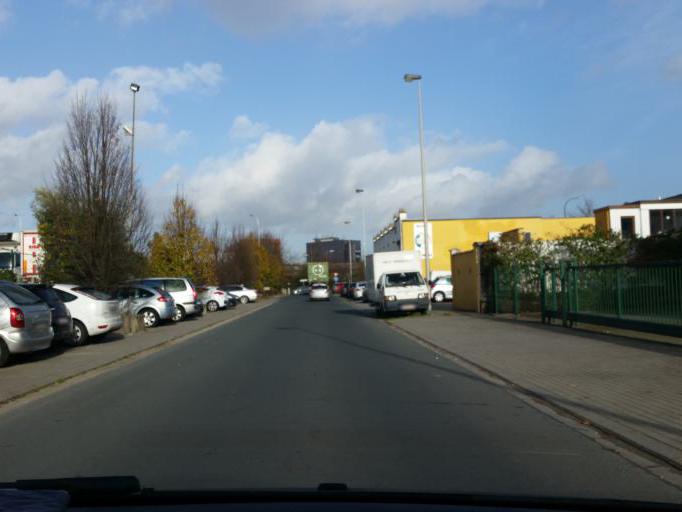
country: BE
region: Flanders
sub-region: Provincie Vlaams-Brabant
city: Drogenbos
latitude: 50.8148
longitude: 4.3062
